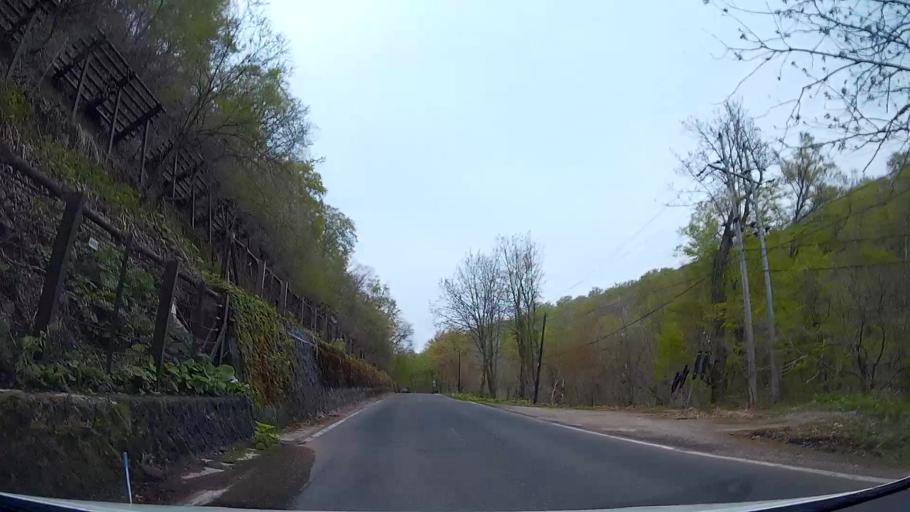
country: JP
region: Akita
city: Hanawa
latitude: 40.3915
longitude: 140.8782
